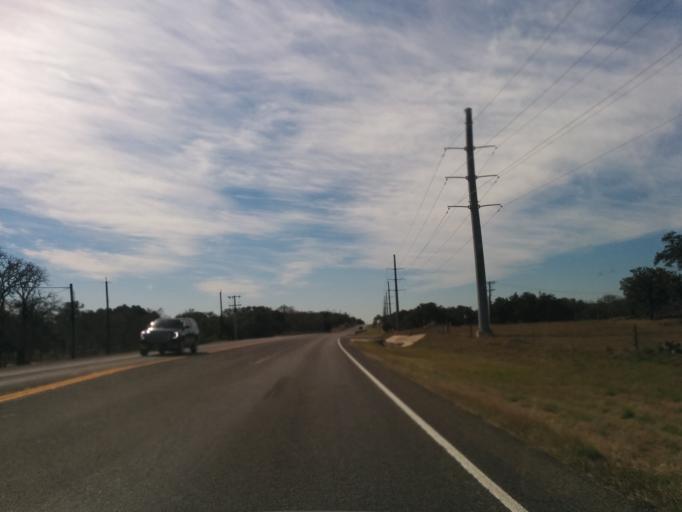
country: US
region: Texas
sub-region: Bexar County
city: Fair Oaks Ranch
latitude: 29.7710
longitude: -98.6043
